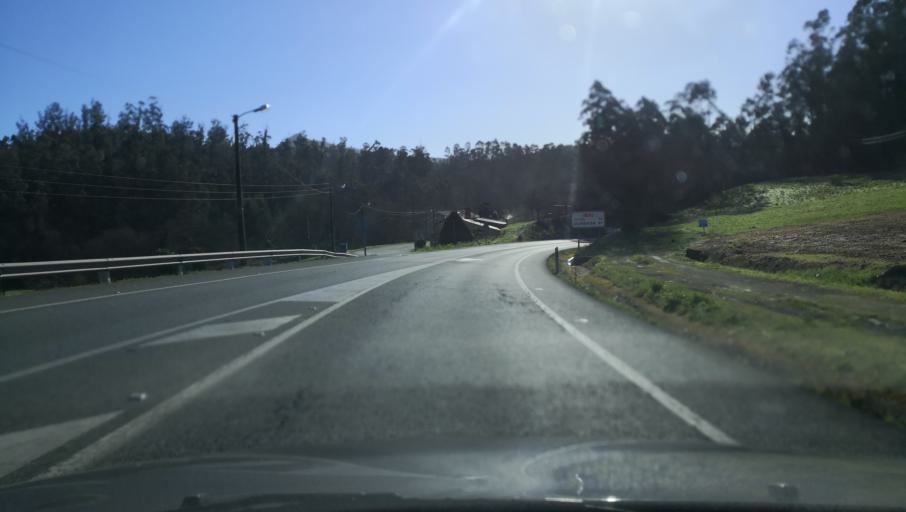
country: ES
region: Galicia
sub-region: Provincia da Coruna
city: Vedra
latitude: 42.8181
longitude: -8.4806
